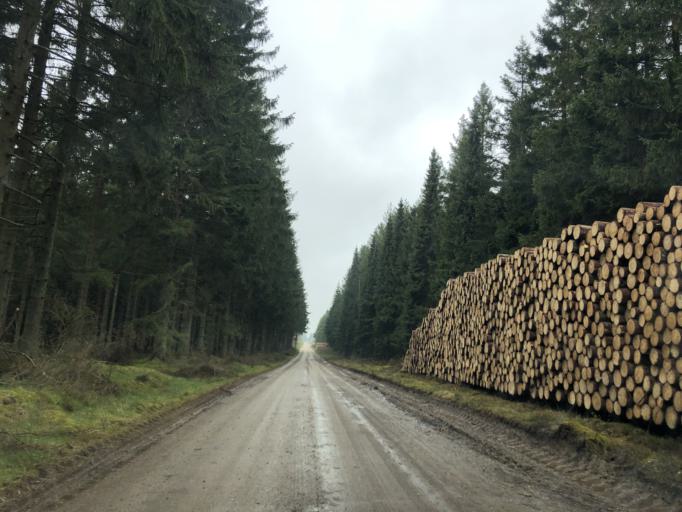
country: DK
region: Central Jutland
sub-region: Lemvig Kommune
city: Lemvig
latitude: 56.4896
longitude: 8.3519
